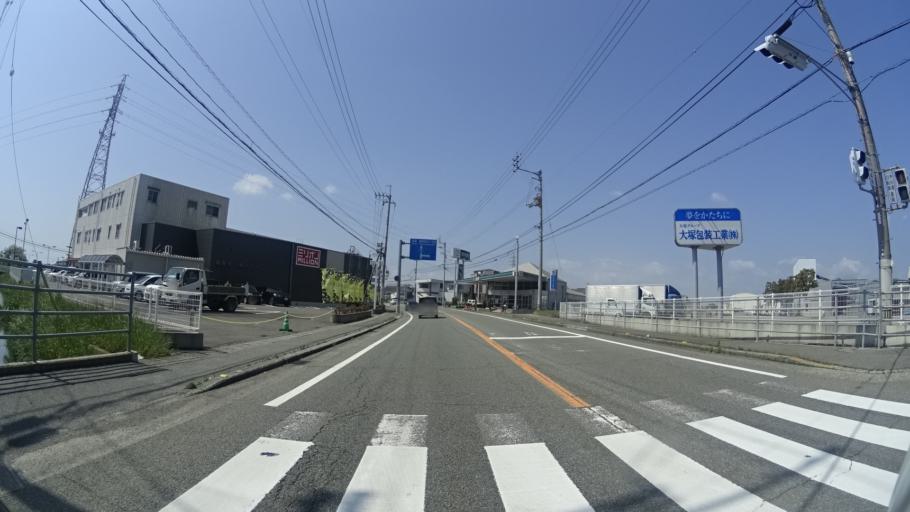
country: JP
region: Tokushima
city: Narutocho-mitsuishi
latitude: 34.1619
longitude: 134.5937
